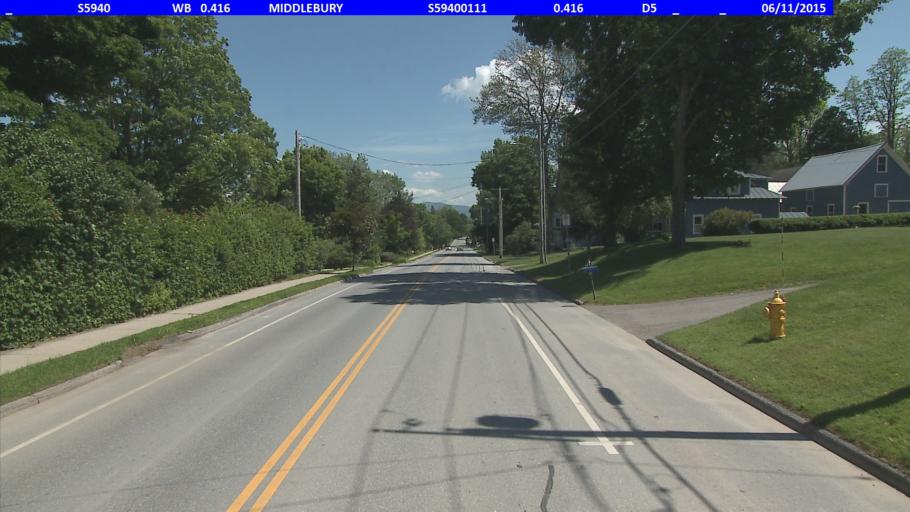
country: US
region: Vermont
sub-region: Addison County
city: Middlebury (village)
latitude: 44.0159
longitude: -73.1770
